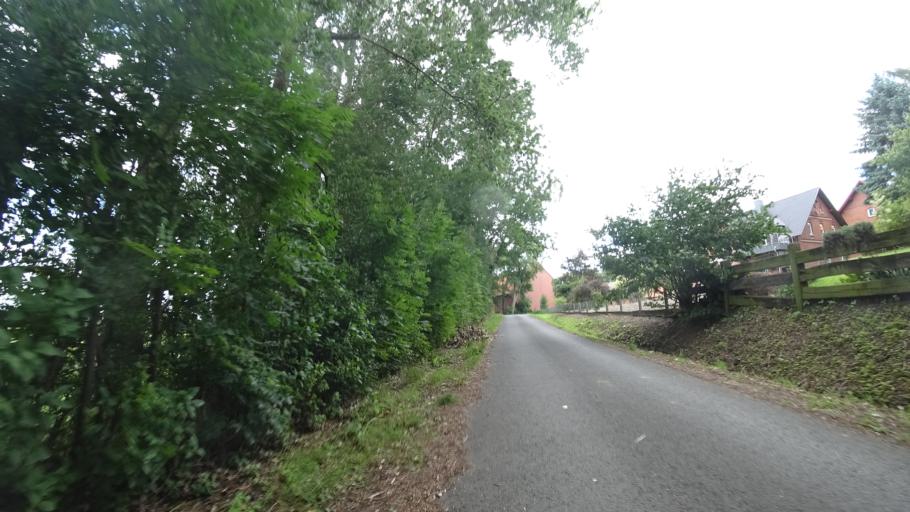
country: DE
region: Lower Saxony
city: Raddestorf
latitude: 52.4560
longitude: 9.0225
